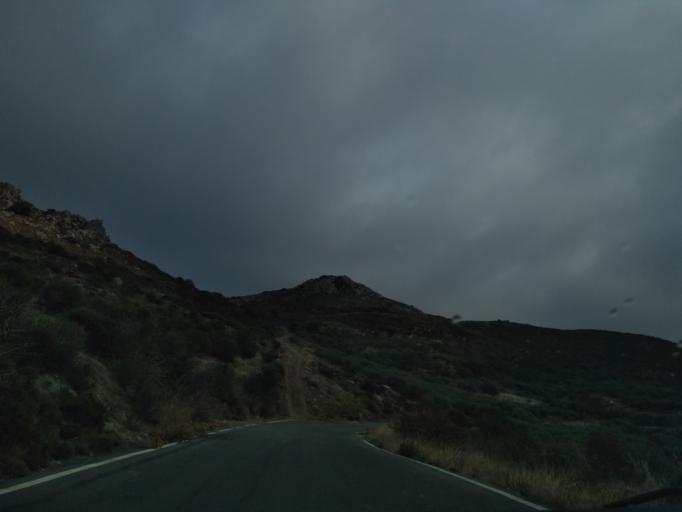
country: GR
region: Crete
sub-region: Nomos Lasithiou
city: Siteia
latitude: 35.1504
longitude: 26.0198
